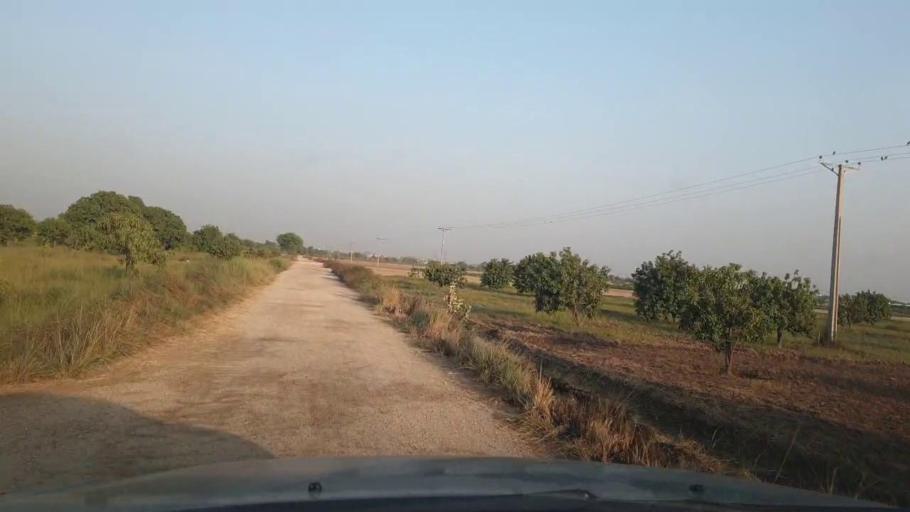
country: PK
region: Sindh
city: Tando Jam
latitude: 25.4267
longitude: 68.5040
